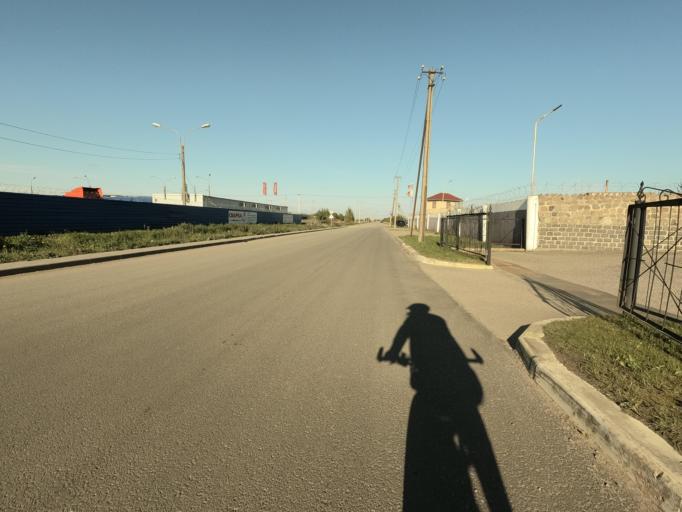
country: RU
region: St.-Petersburg
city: Petro-Slavyanka
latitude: 59.7641
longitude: 30.4844
